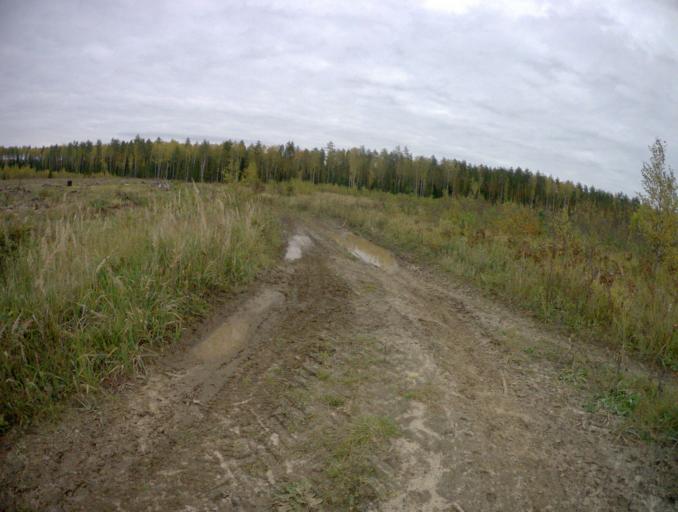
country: RU
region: Vladimir
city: Stepantsevo
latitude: 56.3102
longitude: 41.5613
